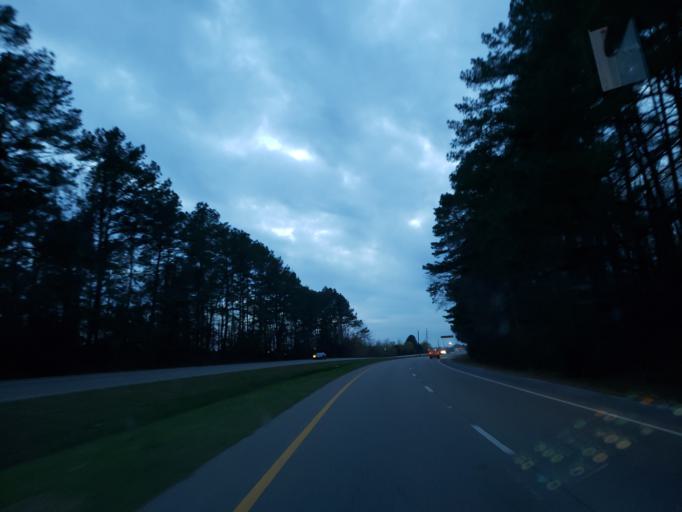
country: US
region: Mississippi
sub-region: Lauderdale County
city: Meridian
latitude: 32.3640
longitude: -88.6613
